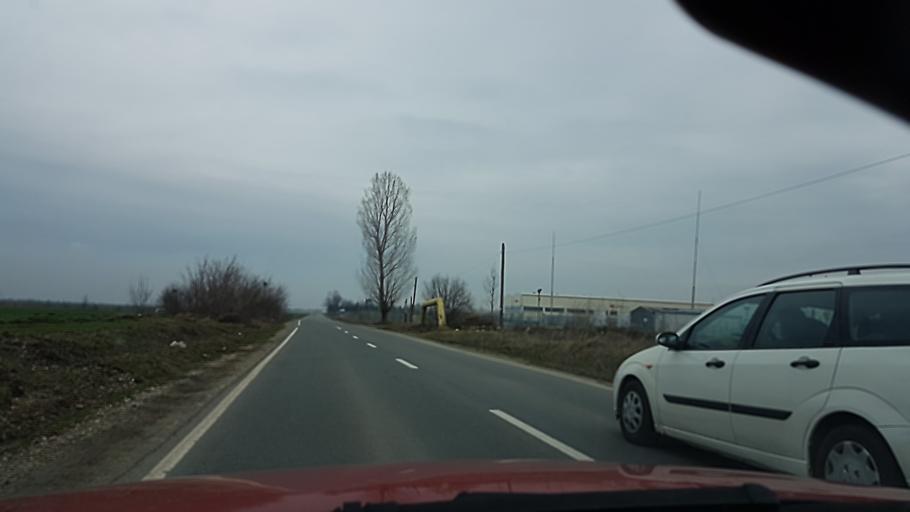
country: RO
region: Ilfov
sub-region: Comuna Balotesti
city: Balotesti
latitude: 44.6131
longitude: 26.1276
